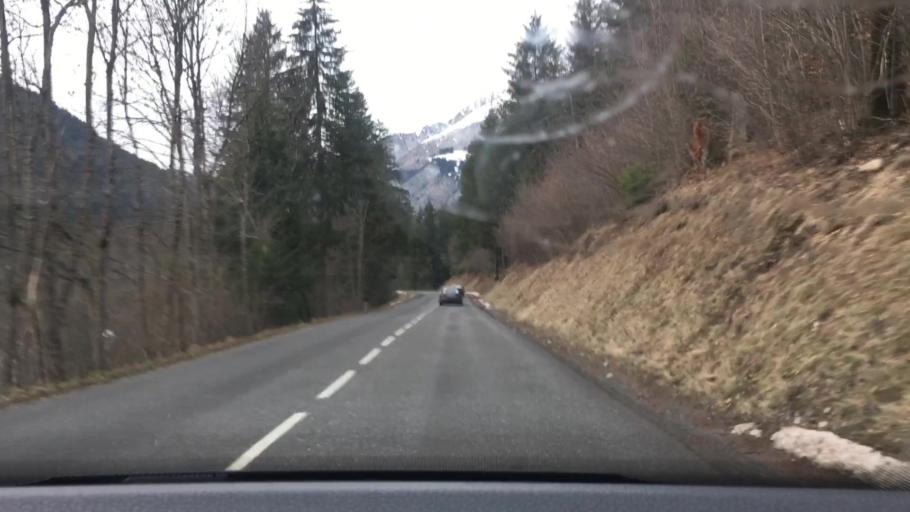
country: FR
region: Rhone-Alpes
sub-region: Departement de la Haute-Savoie
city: Chatel
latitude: 46.2816
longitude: 6.8220
